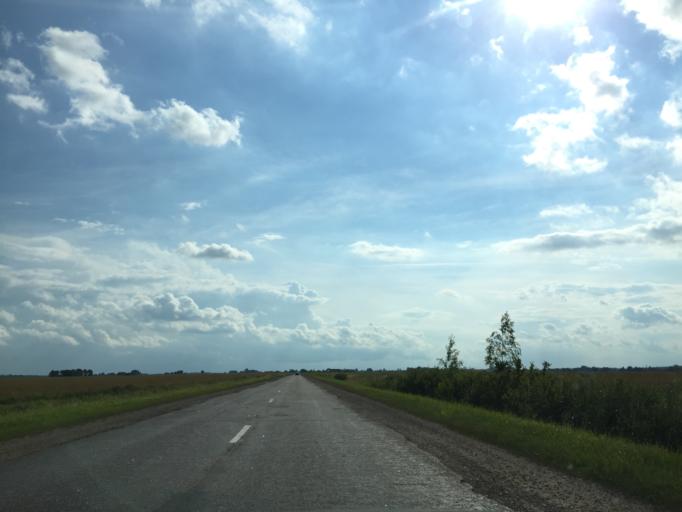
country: LV
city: Tervete
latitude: 56.5737
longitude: 23.4255
